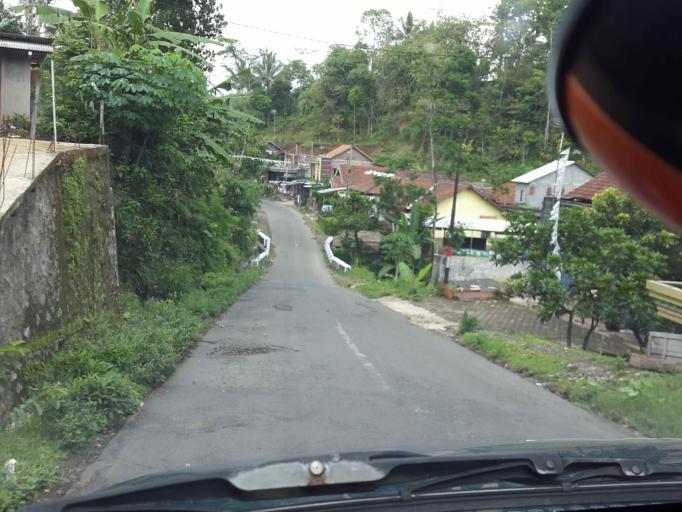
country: ID
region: Central Java
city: Magelang
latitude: -7.5213
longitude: 110.0567
